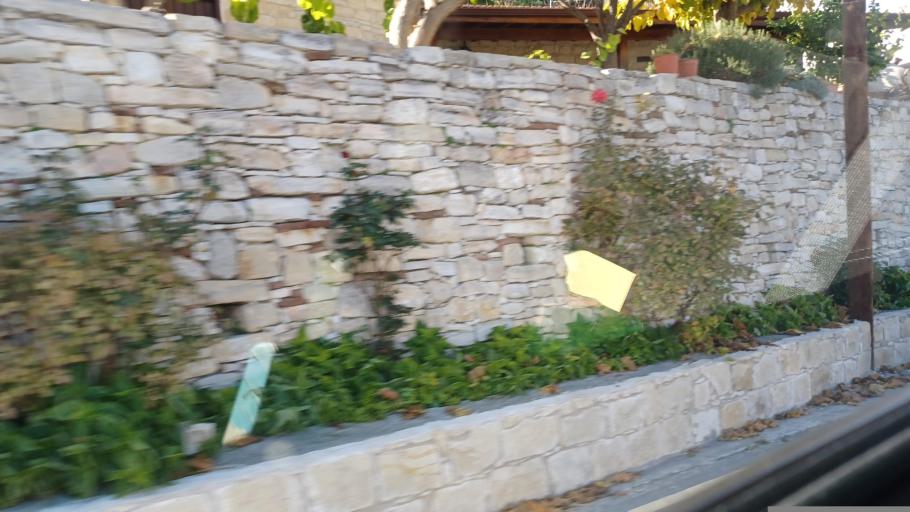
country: CY
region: Limassol
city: Pachna
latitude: 34.8350
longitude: 32.7935
